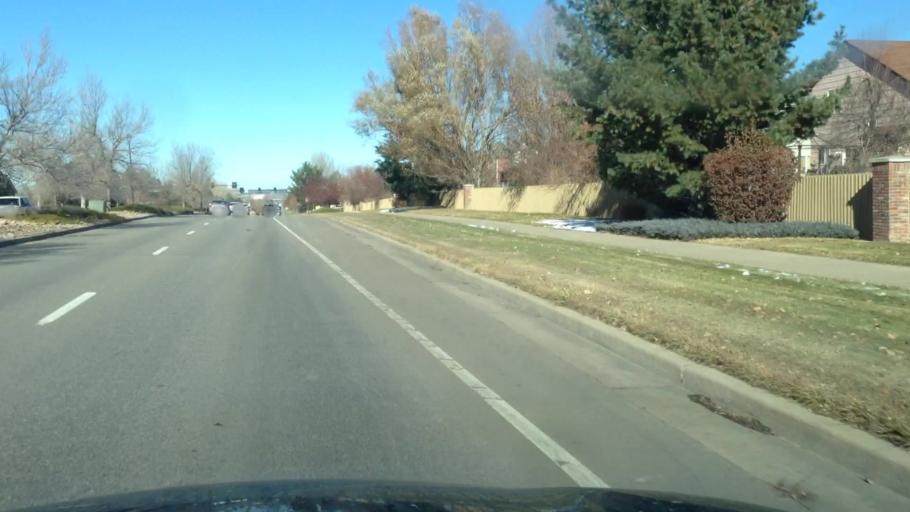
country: US
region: Colorado
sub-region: Douglas County
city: Stonegate
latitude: 39.5161
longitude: -104.7933
